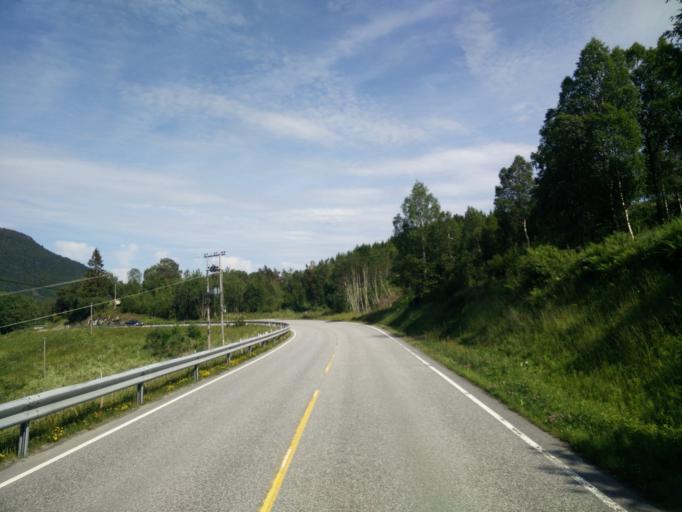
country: NO
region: More og Romsdal
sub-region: Tingvoll
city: Tingvoll
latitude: 63.0435
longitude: 8.0573
